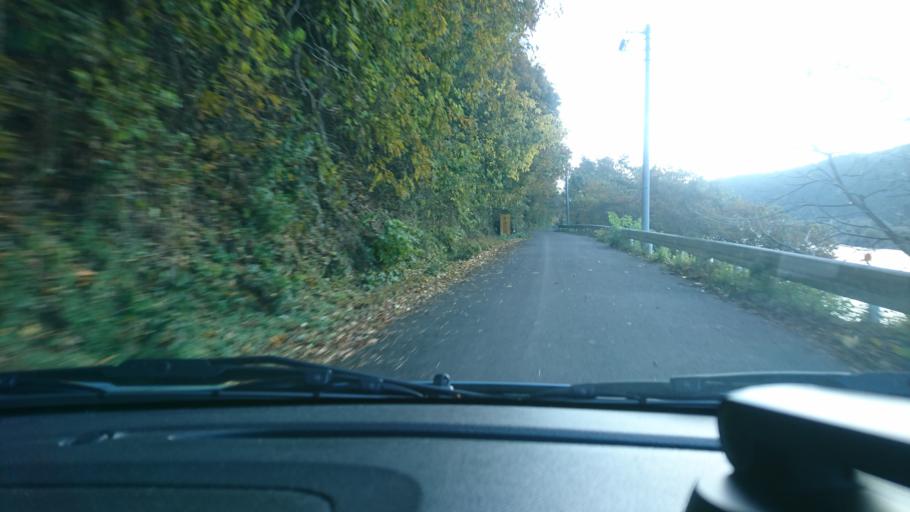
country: JP
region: Iwate
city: Ichinoseki
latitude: 38.8110
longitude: 141.2516
